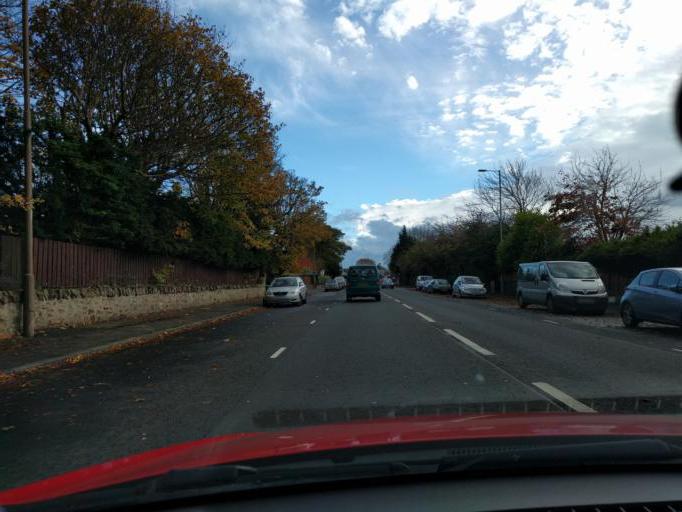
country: GB
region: Scotland
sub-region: Edinburgh
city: Edinburgh
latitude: 55.9101
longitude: -3.2109
